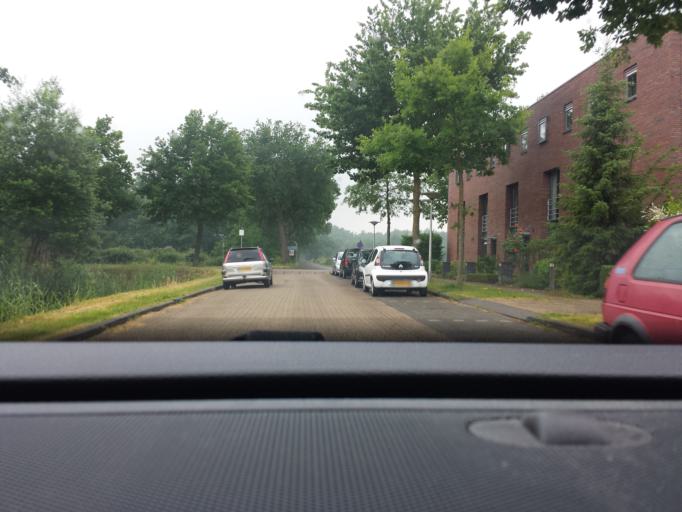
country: NL
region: Overijssel
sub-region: Gemeente Enschede
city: Enschede
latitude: 52.2128
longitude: 6.9426
